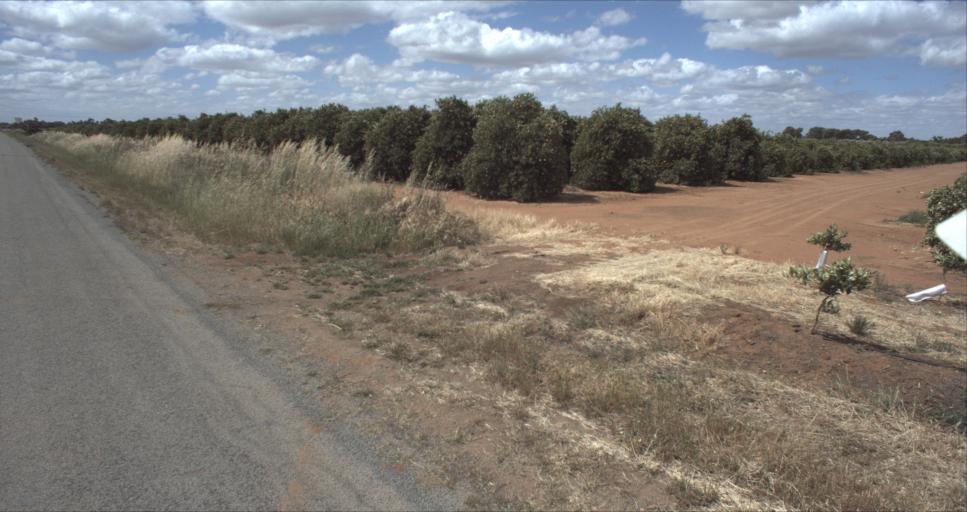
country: AU
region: New South Wales
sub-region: Leeton
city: Leeton
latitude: -34.5825
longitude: 146.3920
